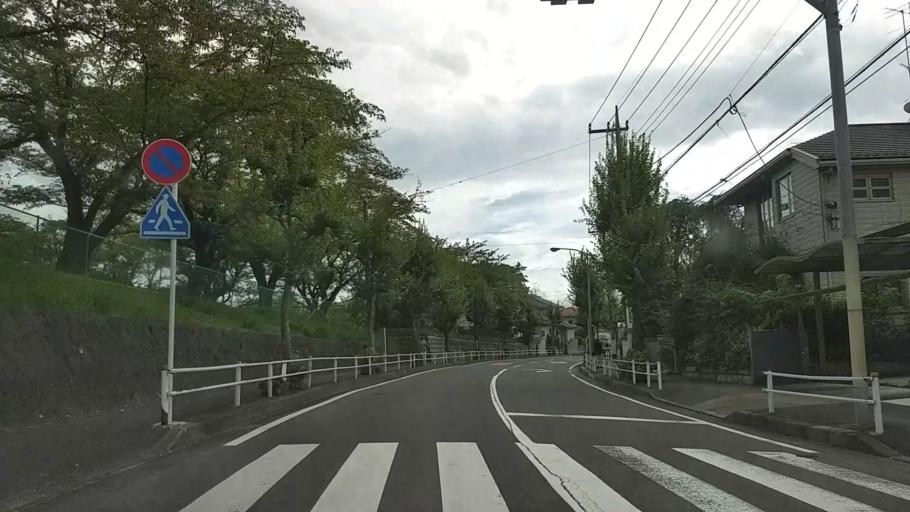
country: JP
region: Tokyo
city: Hachioji
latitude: 35.6302
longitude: 139.3577
